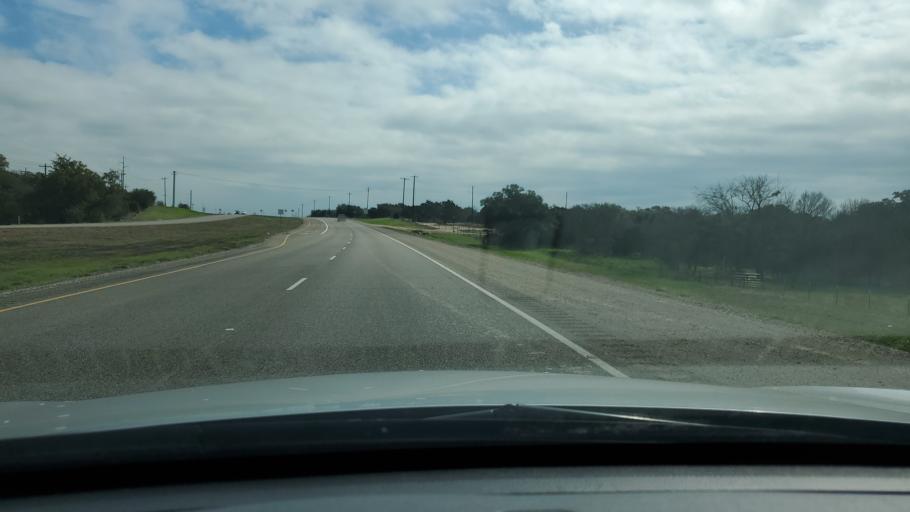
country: US
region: Texas
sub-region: Williamson County
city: Serenada
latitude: 30.7624
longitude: -97.7450
